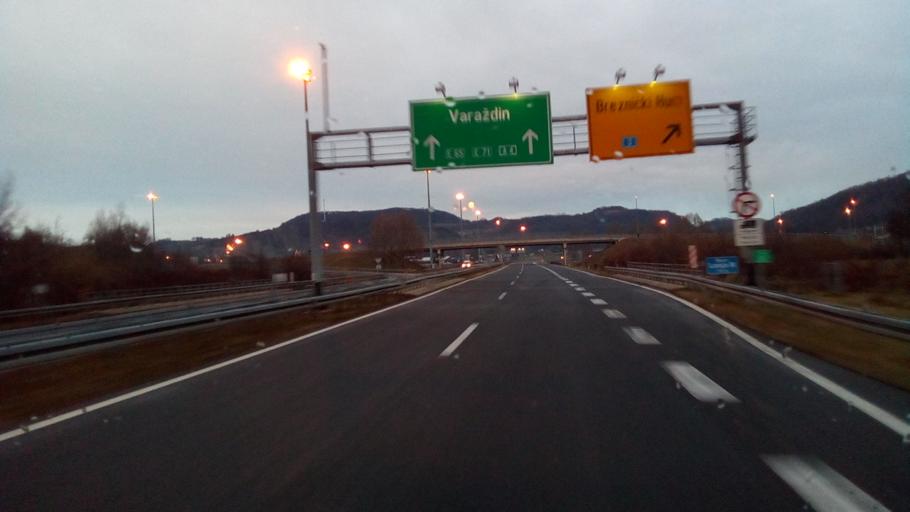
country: HR
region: Varazdinska
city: Remetinec
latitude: 46.0968
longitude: 16.2838
